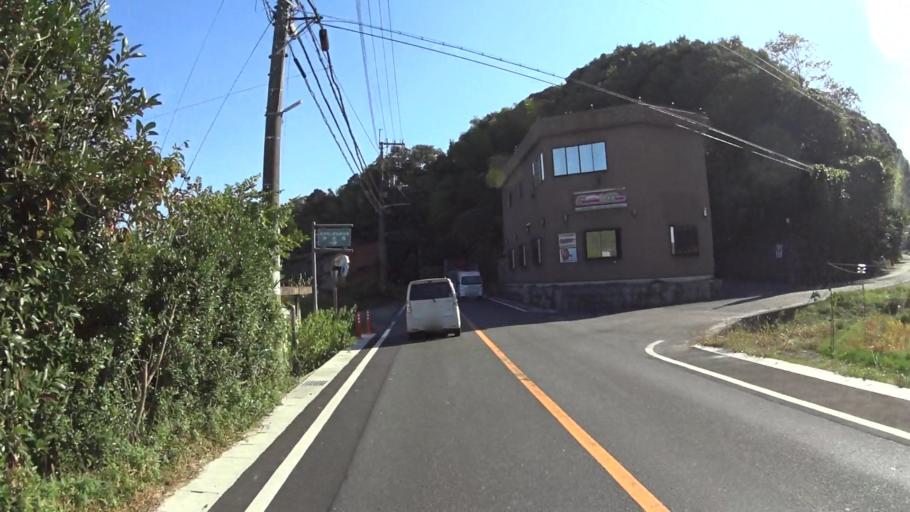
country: JP
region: Kyoto
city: Miyazu
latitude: 35.6652
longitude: 135.0284
